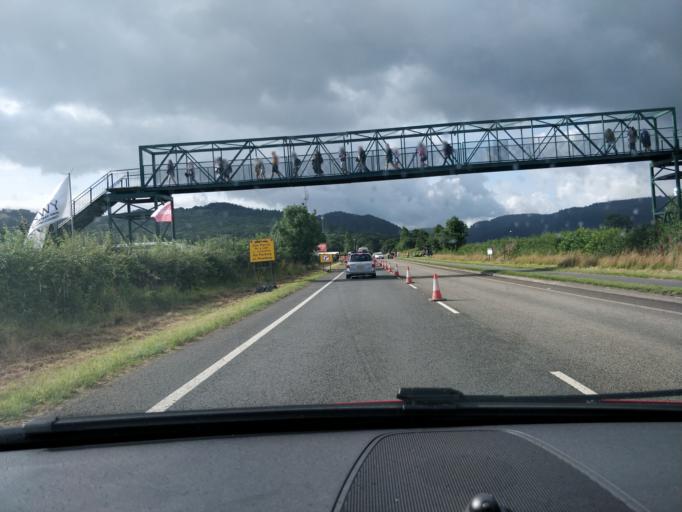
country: GB
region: Wales
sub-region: Conwy
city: Llanrwst
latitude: 53.1145
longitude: -3.7815
